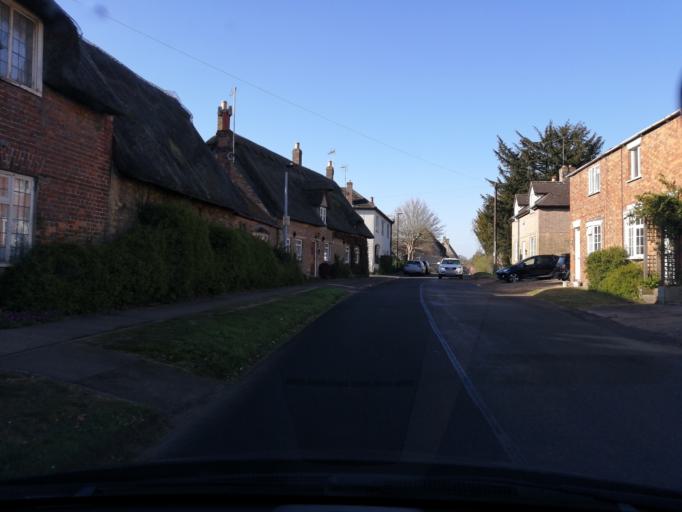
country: GB
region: England
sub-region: Cambridgeshire
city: Yaxley
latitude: 52.5532
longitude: -0.2952
